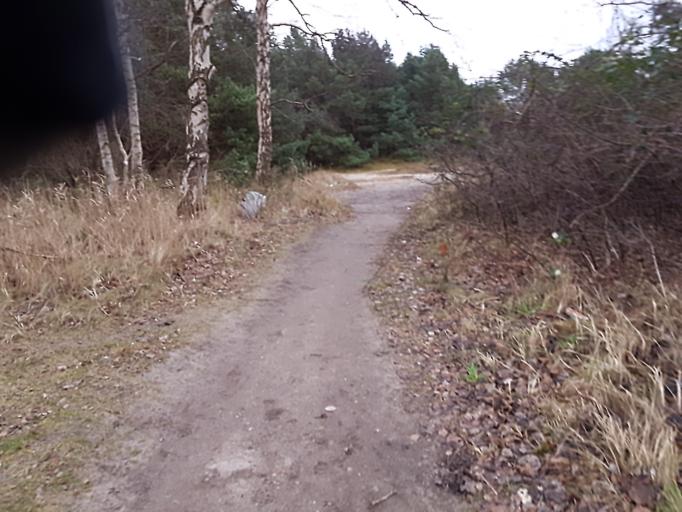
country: DE
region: Mecklenburg-Vorpommern
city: Ostseebad Binz
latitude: 54.4428
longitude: 13.5733
